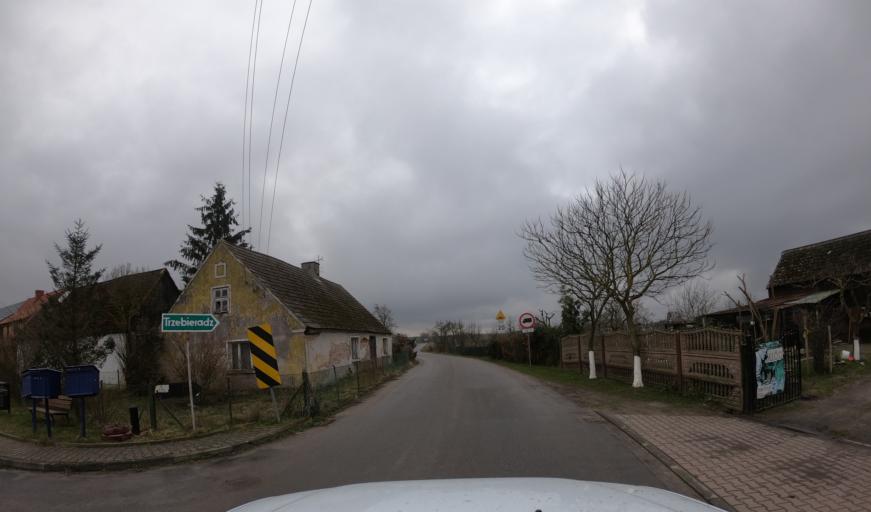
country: PL
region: West Pomeranian Voivodeship
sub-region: Powiat gryficki
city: Pobierowo
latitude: 54.0300
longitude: 14.9523
